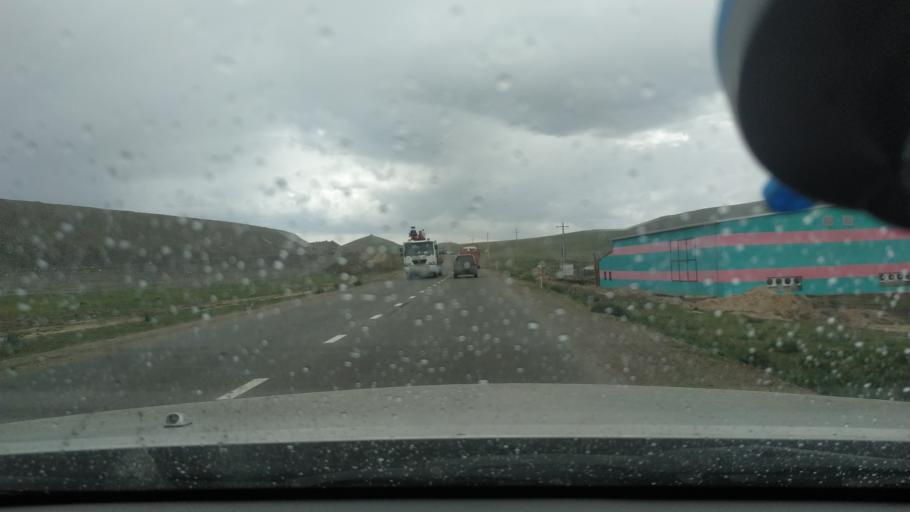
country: MN
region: Ulaanbaatar
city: Ulaanbaatar
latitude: 47.7968
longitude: 106.7456
